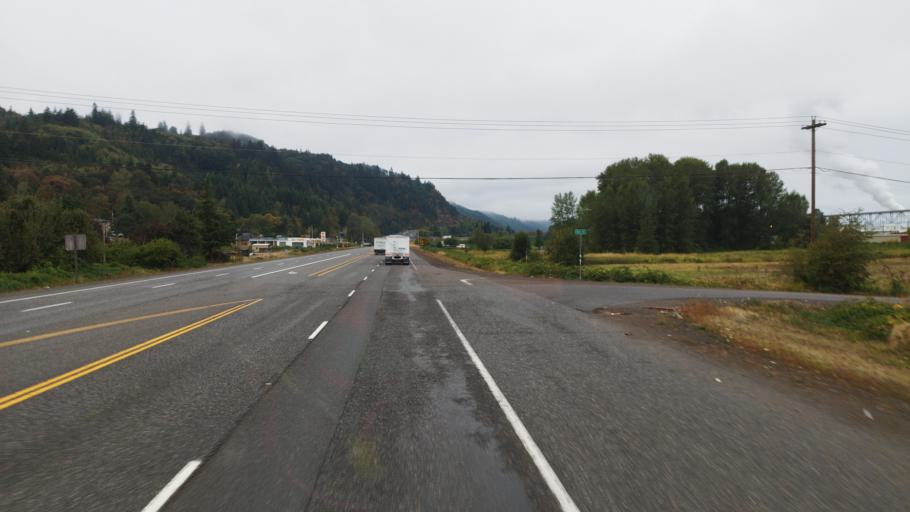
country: US
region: Oregon
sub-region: Columbia County
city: Rainier
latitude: 46.0945
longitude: -122.9579
